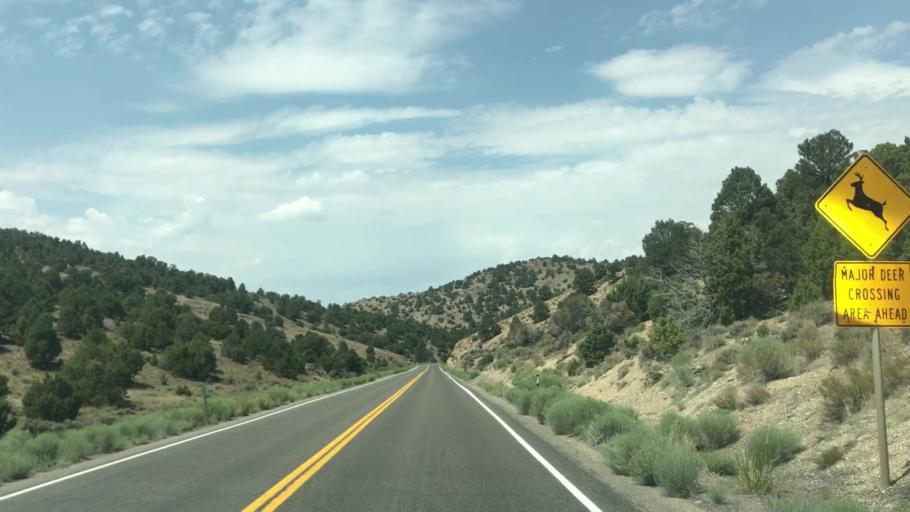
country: US
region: Nevada
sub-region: Eureka County
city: Eureka
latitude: 39.3952
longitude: -115.4802
